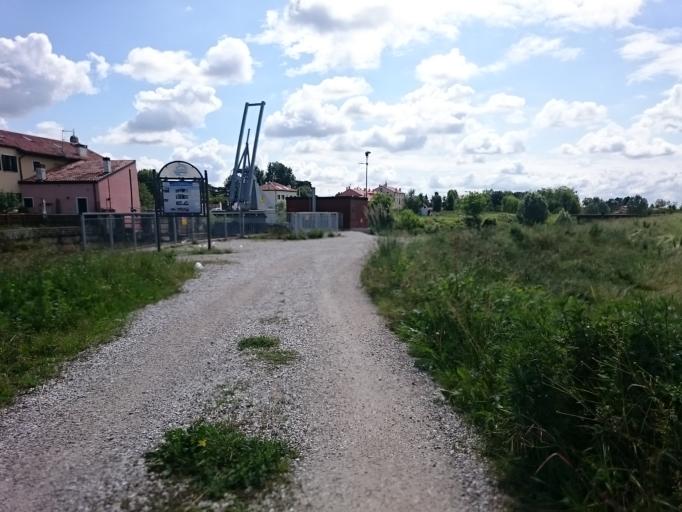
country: IT
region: Veneto
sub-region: Provincia di Padova
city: Arlesega
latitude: 45.4608
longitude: 11.7170
